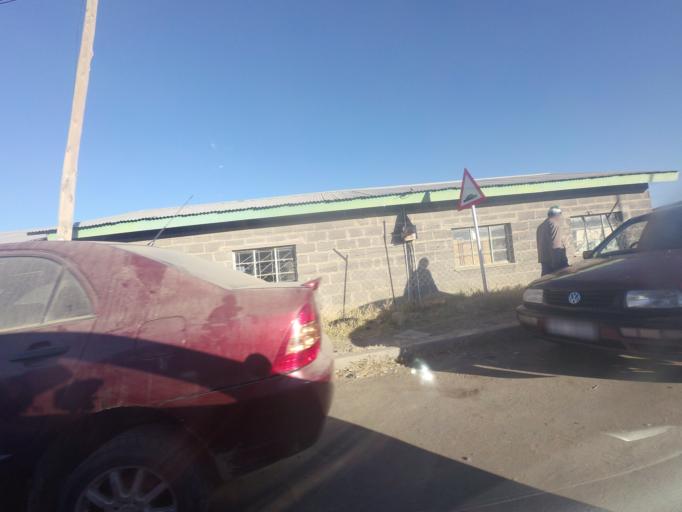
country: LS
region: Maseru
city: Maseru
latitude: -29.3392
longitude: 27.5134
